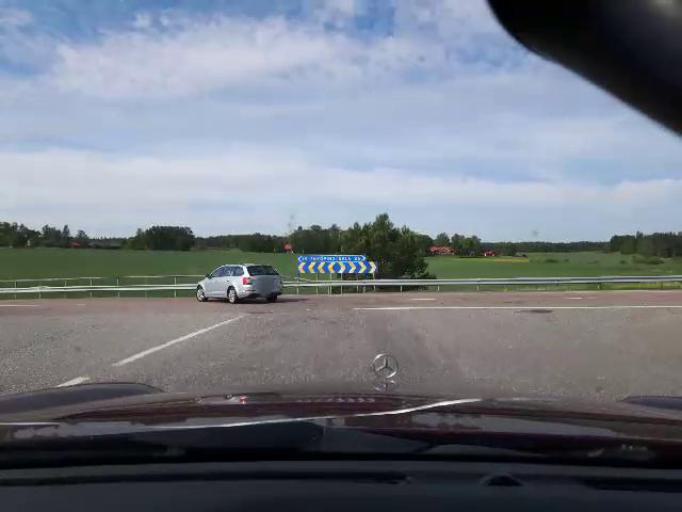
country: SE
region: Uppsala
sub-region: Enkopings Kommun
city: Irsta
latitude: 59.7700
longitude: 16.9120
